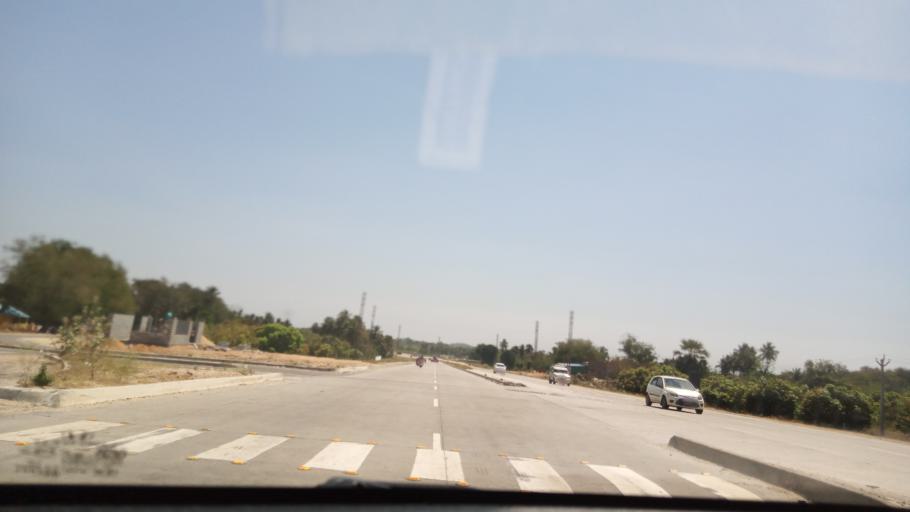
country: IN
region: Andhra Pradesh
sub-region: Chittoor
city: Chittoor
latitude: 13.1968
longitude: 78.9843
